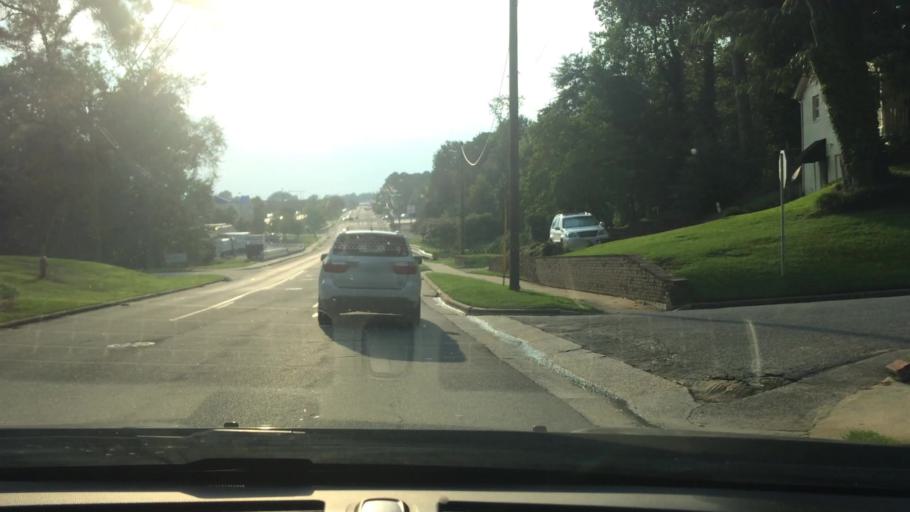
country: US
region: North Carolina
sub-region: Pitt County
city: Greenville
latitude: 35.6004
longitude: -77.3671
